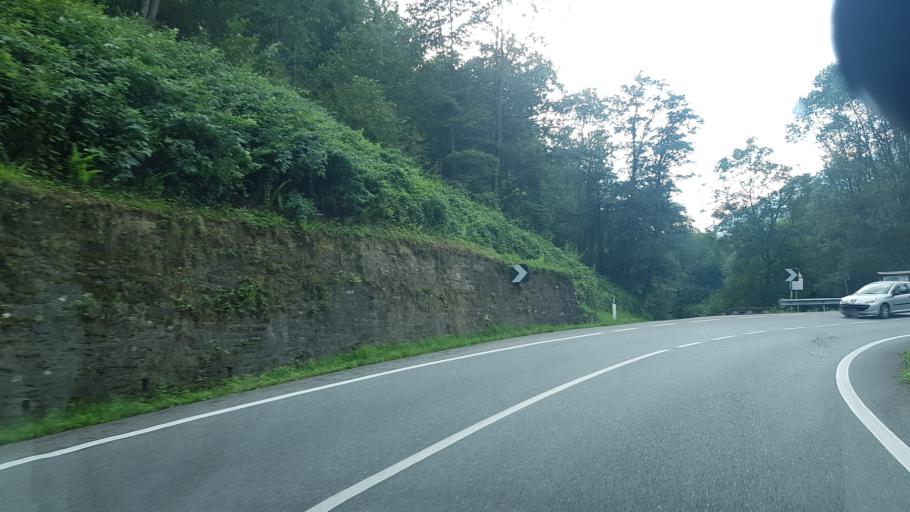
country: IT
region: Piedmont
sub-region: Provincia di Cuneo
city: Frassino
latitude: 44.5691
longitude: 7.2860
